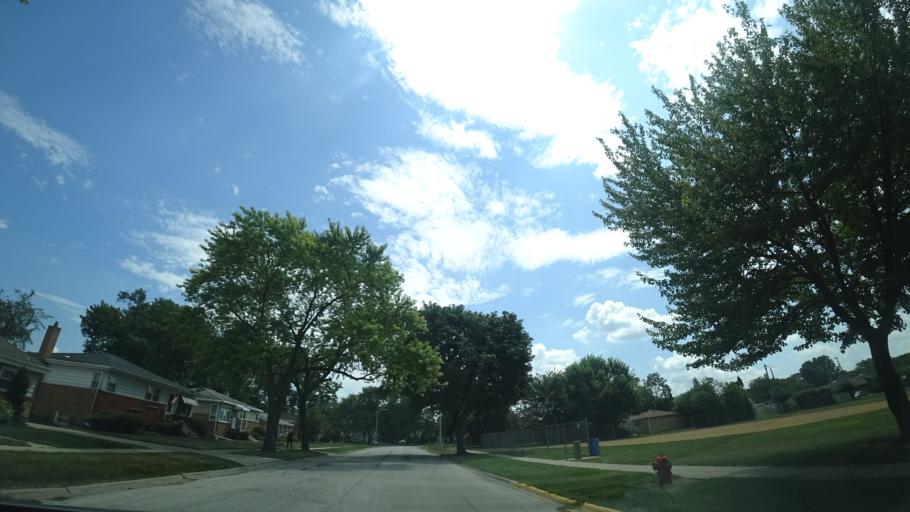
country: US
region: Illinois
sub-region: Cook County
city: Alsip
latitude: 41.6789
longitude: -87.7285
